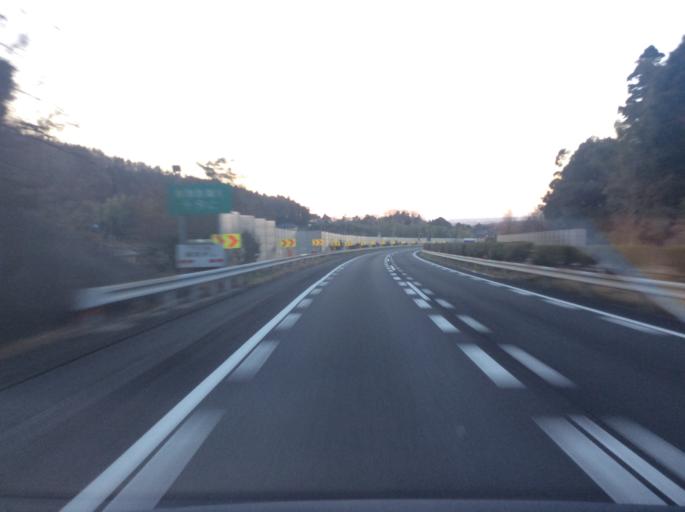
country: JP
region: Ibaraki
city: Funaishikawa
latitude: 36.5275
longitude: 140.5917
